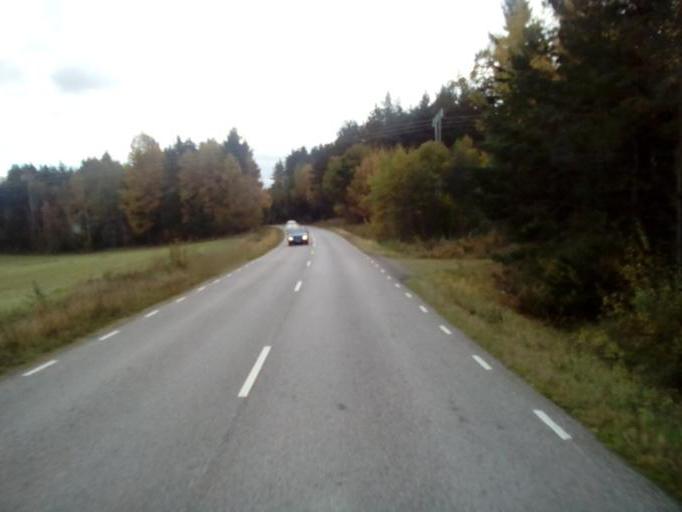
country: SE
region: Kalmar
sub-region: Vasterviks Kommun
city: Gamleby
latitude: 57.8869
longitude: 16.3456
